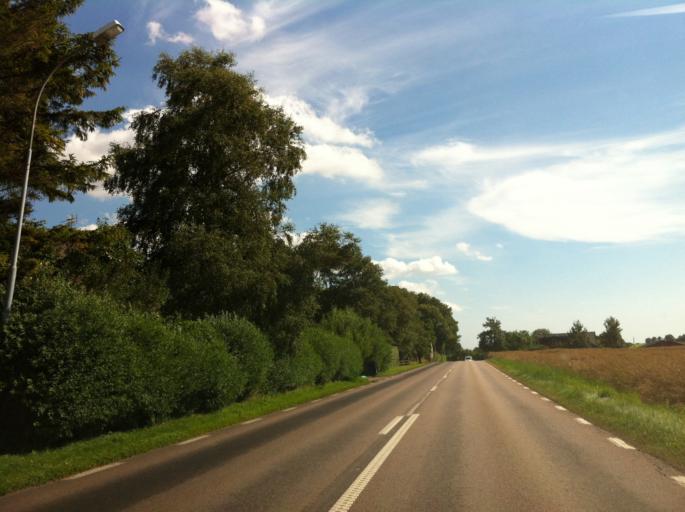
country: SE
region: Skane
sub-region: Landskrona
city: Asmundtorp
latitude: 55.9761
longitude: 12.9306
